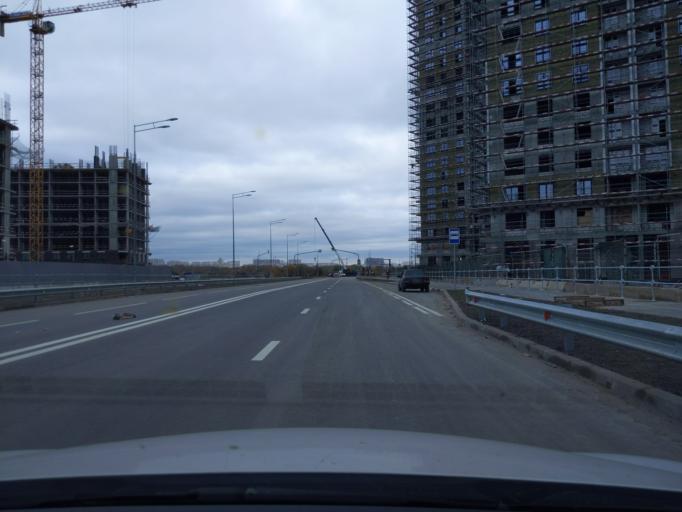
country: RU
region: Moscow
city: Strogino
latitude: 55.8161
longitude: 37.4280
